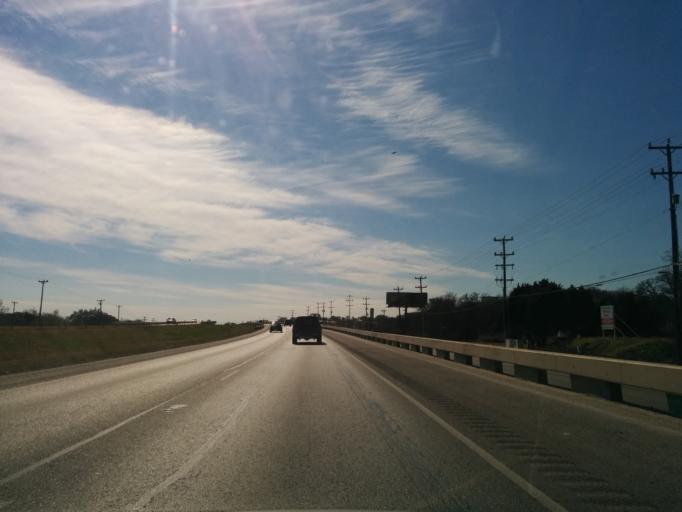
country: US
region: Texas
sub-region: Bexar County
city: Cross Mountain
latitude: 29.6517
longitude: -98.6244
